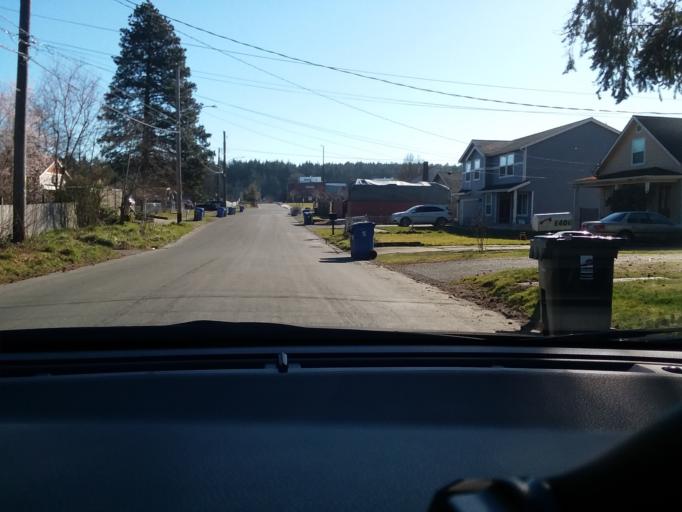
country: US
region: Washington
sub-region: Pierce County
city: Waller
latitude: 47.2099
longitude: -122.4095
